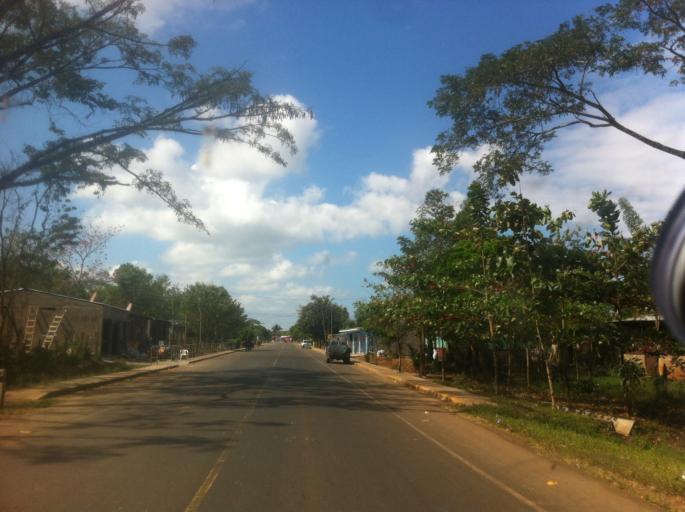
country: NI
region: Rio San Juan
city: San Carlos
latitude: 11.1969
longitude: -84.7395
